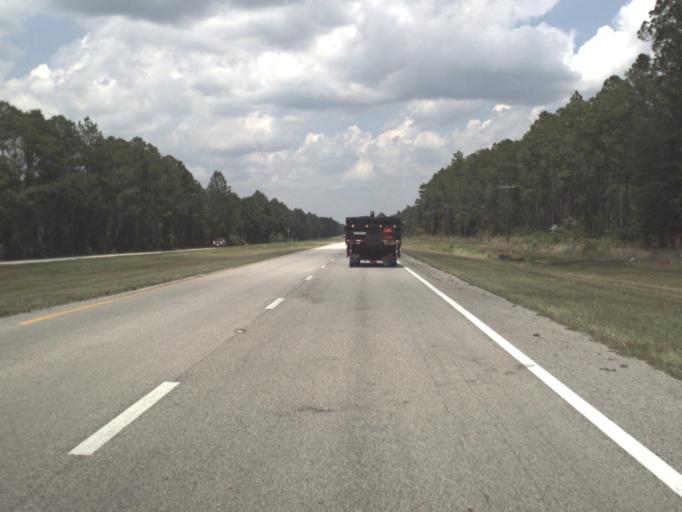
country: US
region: Florida
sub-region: Alachua County
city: Waldo
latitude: 29.7583
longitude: -82.2106
